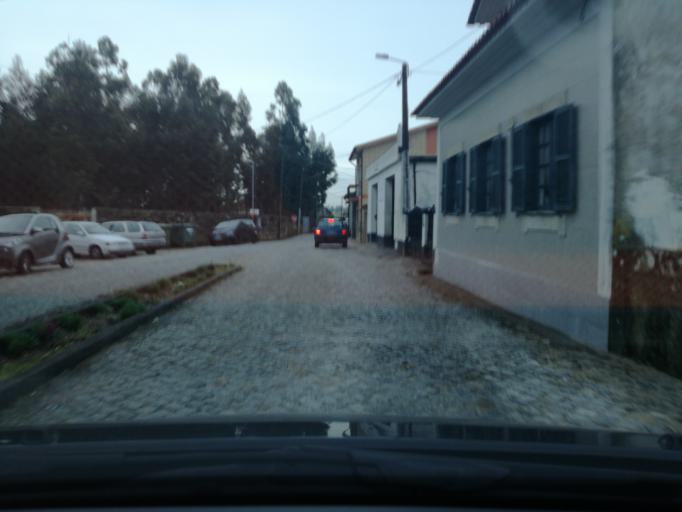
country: PT
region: Porto
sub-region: Maia
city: Gemunde
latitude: 41.2622
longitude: -8.6646
